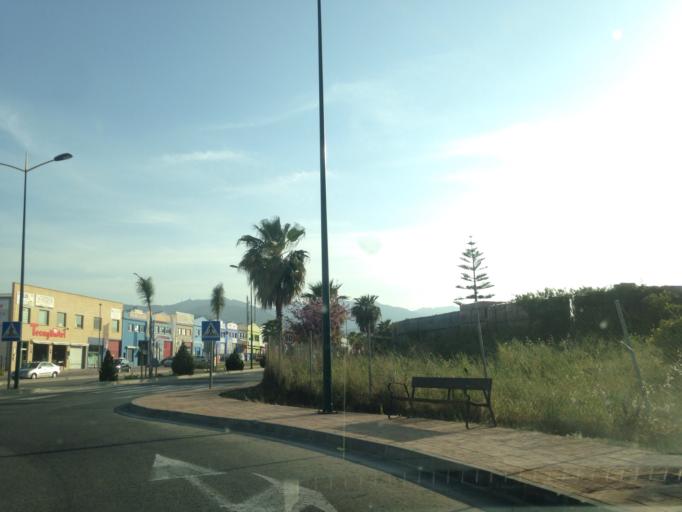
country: ES
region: Andalusia
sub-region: Provincia de Malaga
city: Alhaurin de la Torre
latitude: 36.6768
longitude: -4.5459
